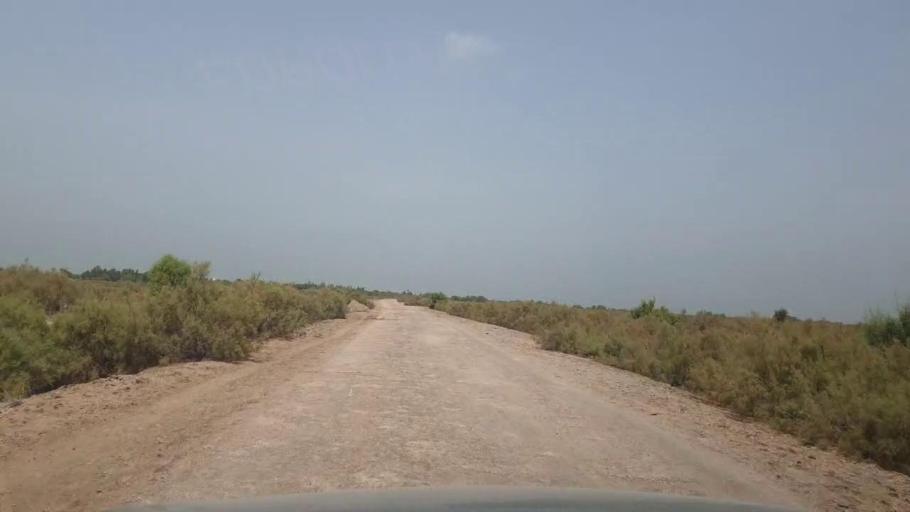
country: PK
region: Sindh
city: Garhi Yasin
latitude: 27.9141
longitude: 68.3791
